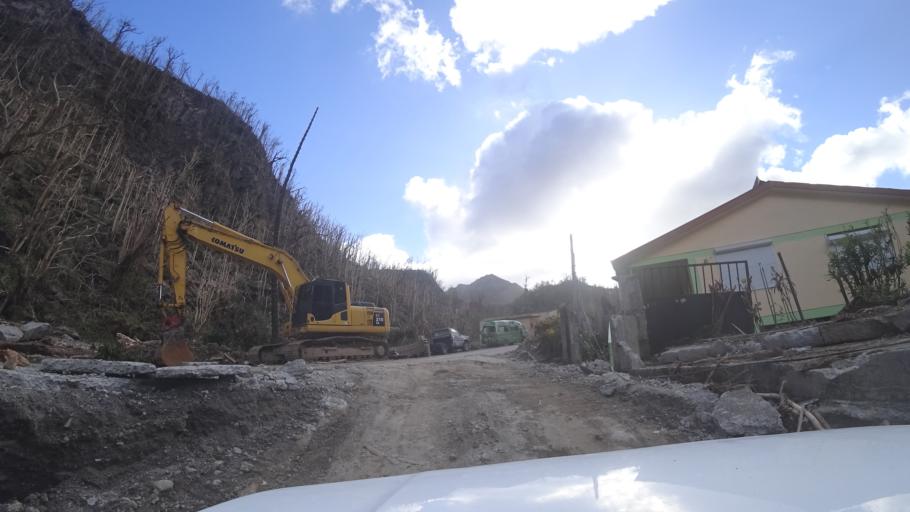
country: DM
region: Saint Patrick
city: Berekua
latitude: 15.2641
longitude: -61.3242
